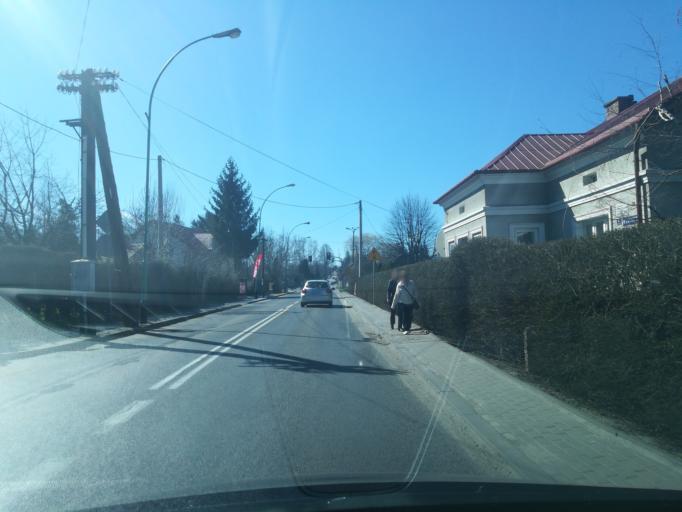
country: PL
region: Subcarpathian Voivodeship
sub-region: Powiat lancucki
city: Lancut
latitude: 50.0633
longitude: 22.2286
